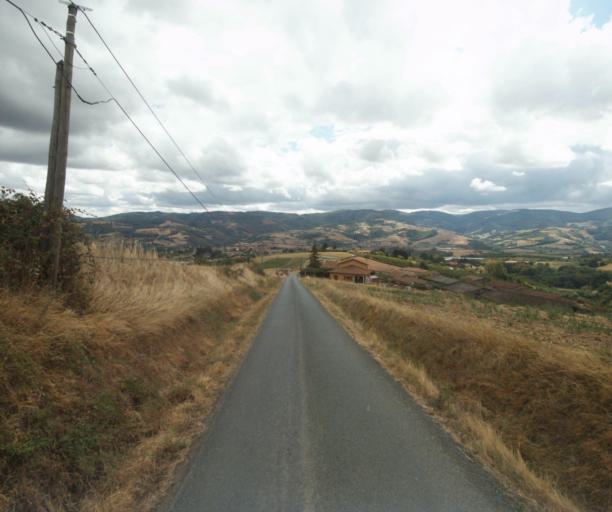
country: FR
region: Rhone-Alpes
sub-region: Departement du Rhone
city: Bessenay
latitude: 45.7821
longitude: 4.5360
